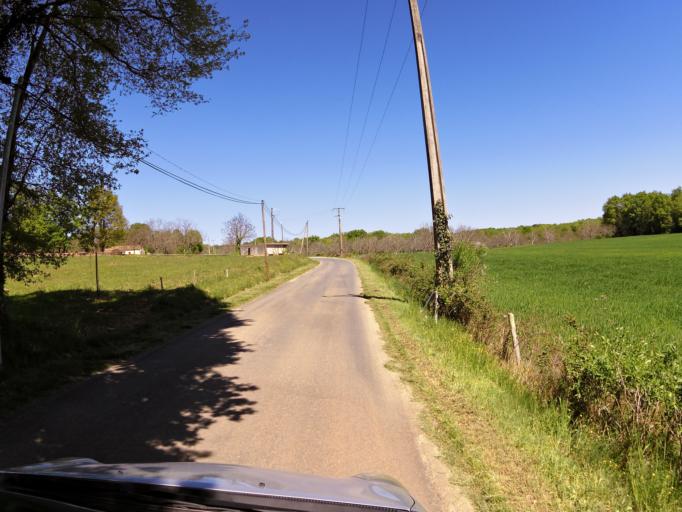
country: FR
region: Aquitaine
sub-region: Departement de la Dordogne
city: Eyvigues-et-Eybenes
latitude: 44.9133
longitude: 1.2883
